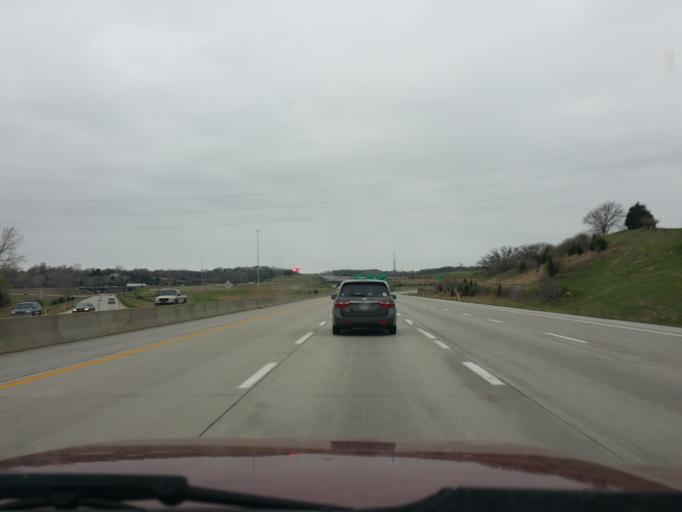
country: US
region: Kansas
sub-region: Wyandotte County
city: Edwardsville
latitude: 39.1060
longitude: -94.8010
